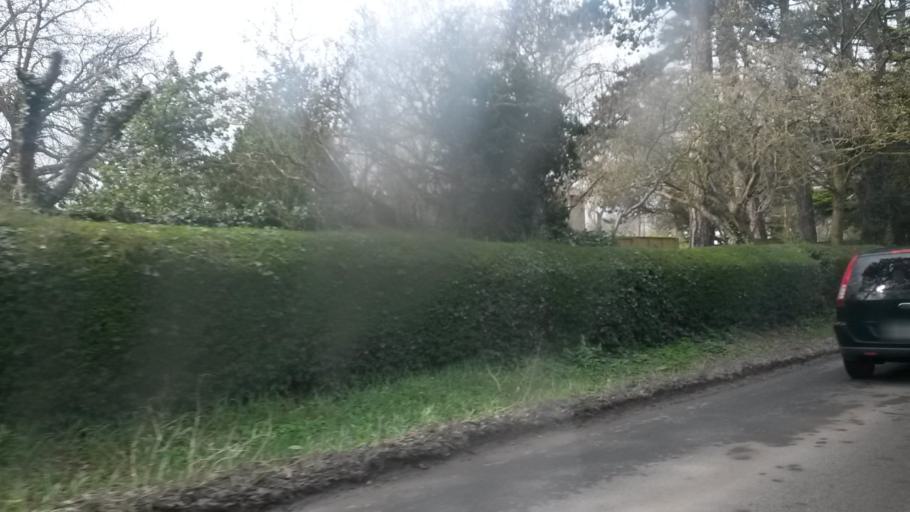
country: IE
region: Leinster
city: Portmarnock
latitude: 53.4192
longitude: -6.1567
